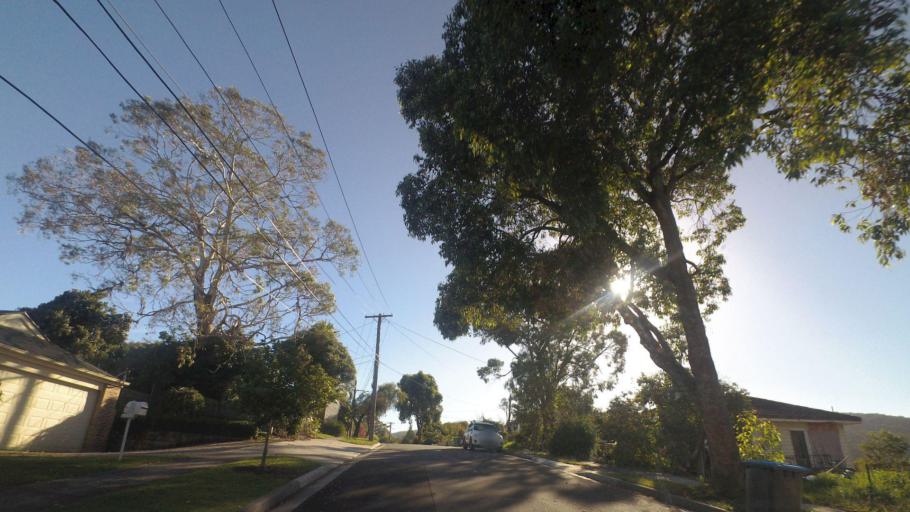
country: AU
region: Victoria
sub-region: Knox
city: Ferntree Gully
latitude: -37.8873
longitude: 145.2893
